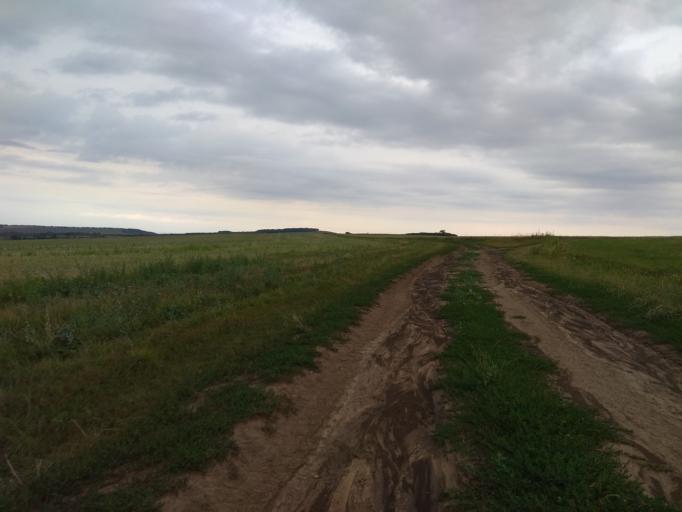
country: HU
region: Borsod-Abauj-Zemplen
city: Megyaszo
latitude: 48.1814
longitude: 21.0994
